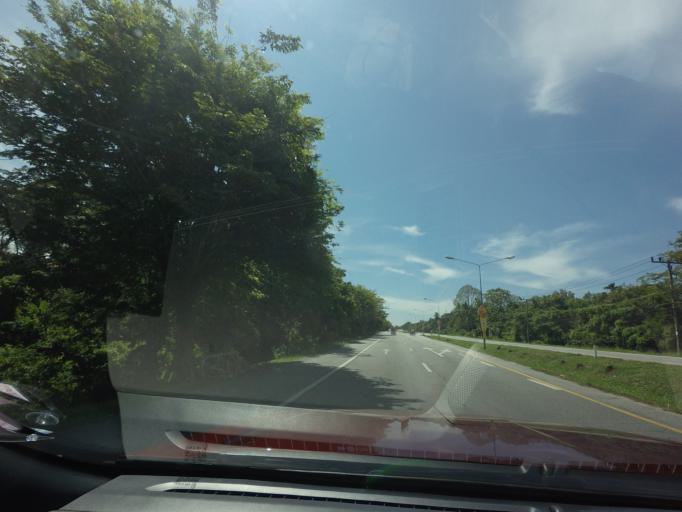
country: TH
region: Pattani
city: Mai Kaen
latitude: 6.6196
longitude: 101.6298
